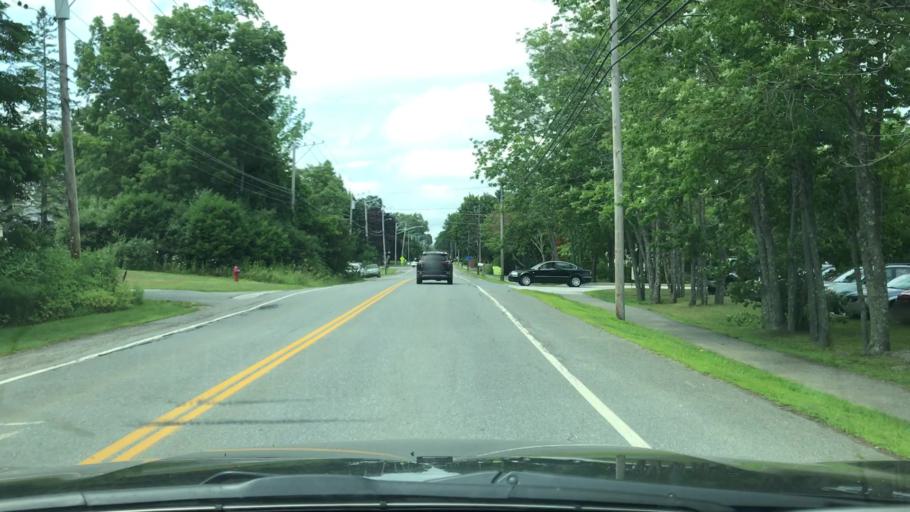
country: US
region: Maine
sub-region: Waldo County
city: Belfast
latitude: 44.4130
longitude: -68.9952
